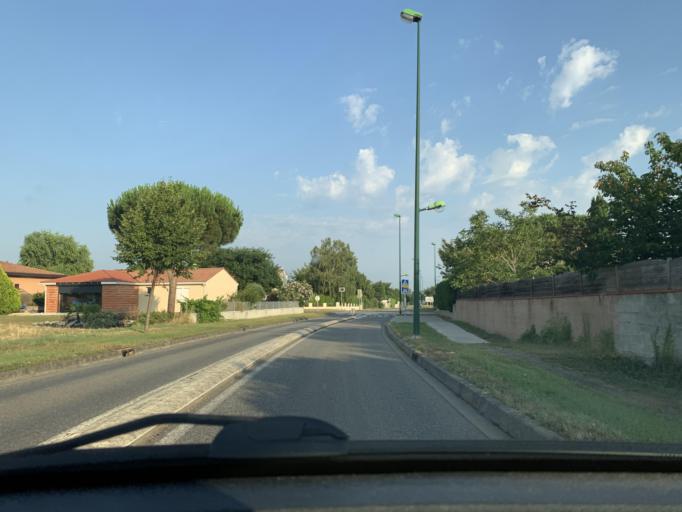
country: FR
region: Midi-Pyrenees
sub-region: Departement de la Haute-Garonne
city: Escalquens
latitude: 43.5294
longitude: 1.5548
